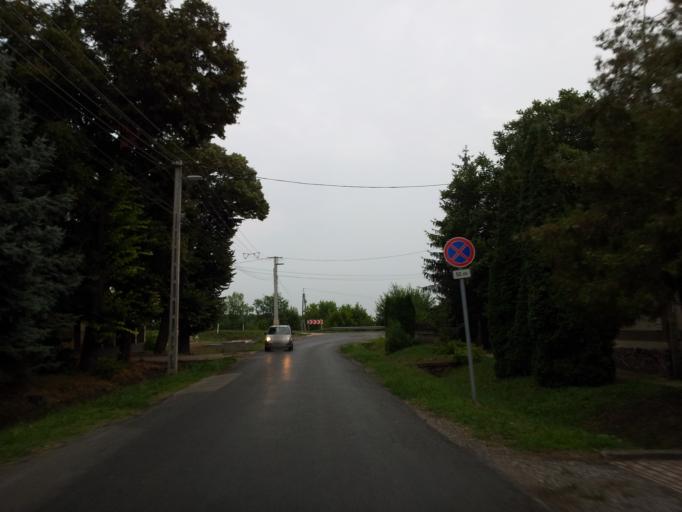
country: HU
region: Tolna
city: Szentgalpuszta
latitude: 46.3895
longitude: 18.6609
